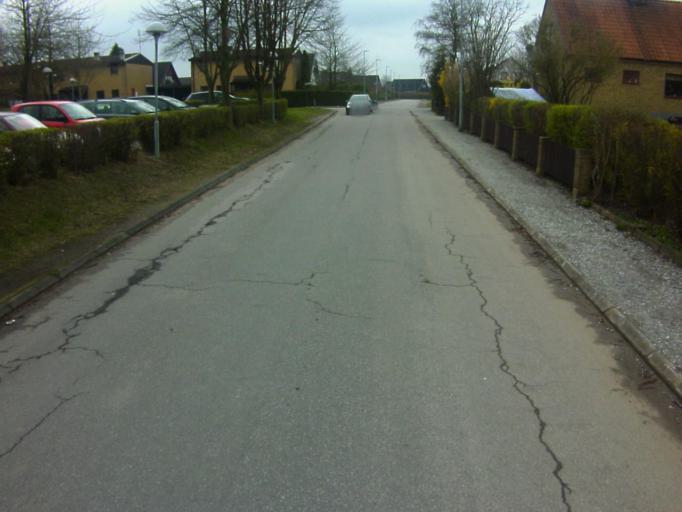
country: SE
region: Skane
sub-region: Kavlinge Kommun
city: Kaevlinge
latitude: 55.7748
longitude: 13.1031
